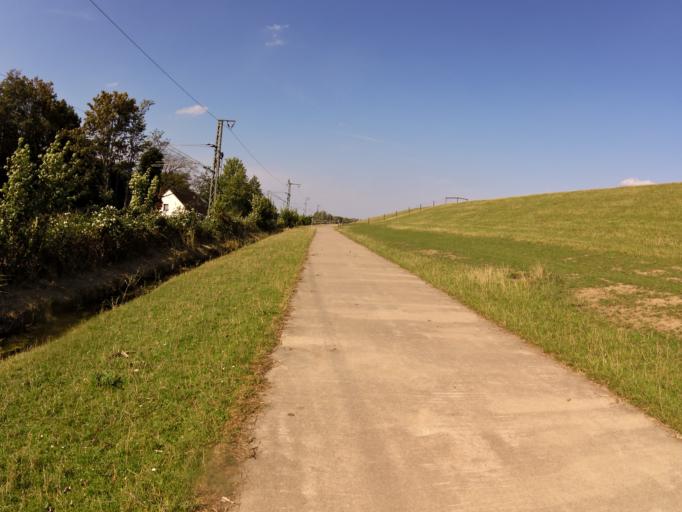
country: DE
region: Lower Saxony
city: Nordenham
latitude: 53.4470
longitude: 8.4759
